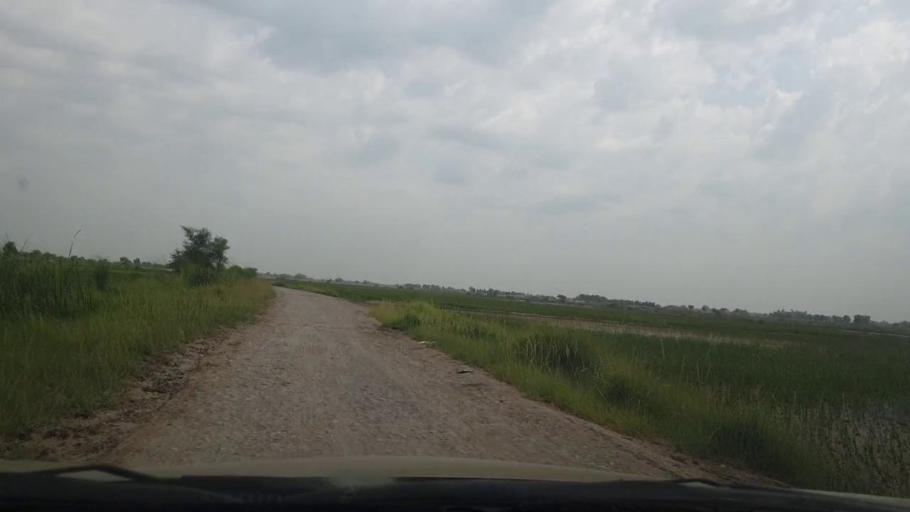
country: PK
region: Sindh
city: Ratodero
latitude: 27.7192
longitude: 68.2309
